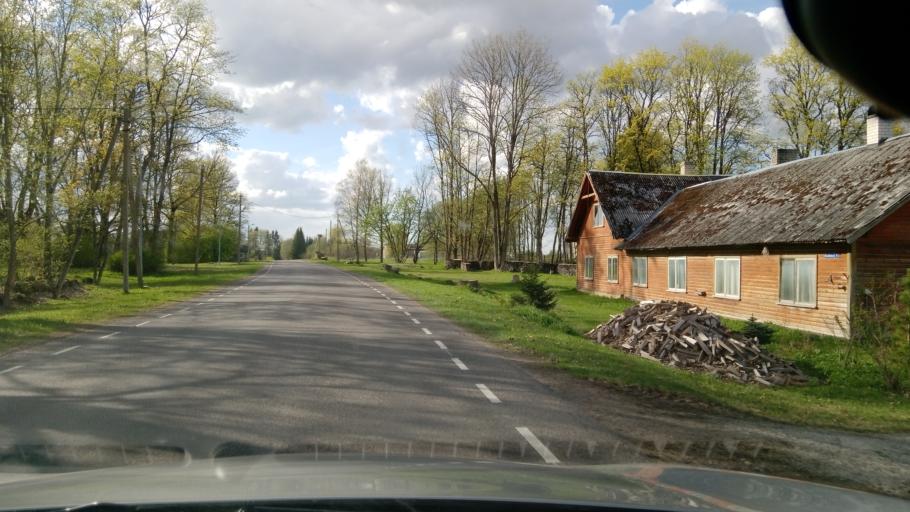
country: EE
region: Jaervamaa
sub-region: Jaerva-Jaani vald
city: Jarva-Jaani
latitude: 58.9446
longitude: 25.8337
